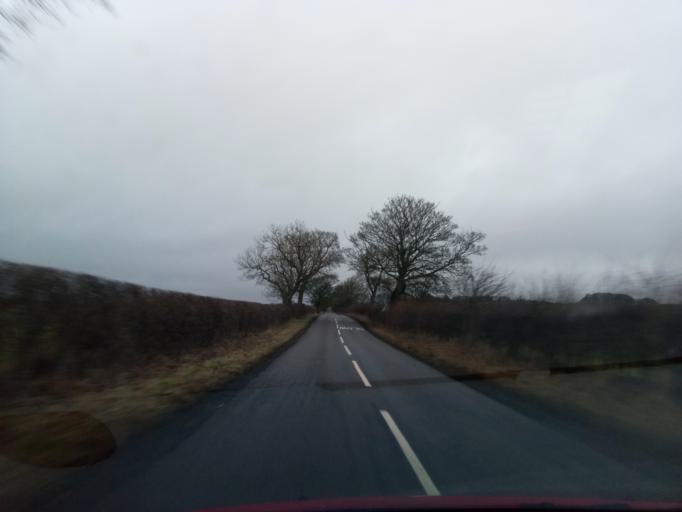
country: GB
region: England
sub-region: Northumberland
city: Rothley
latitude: 55.1873
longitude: -1.9699
